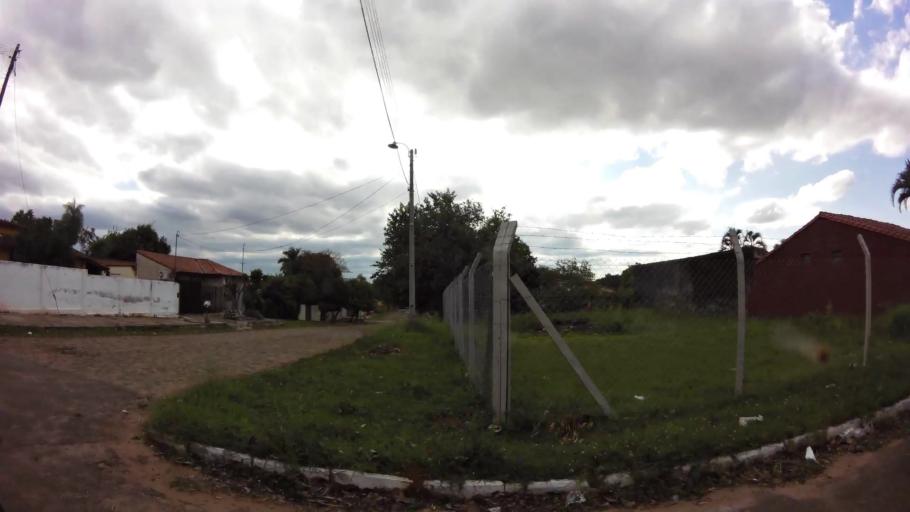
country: PY
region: Central
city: San Lorenzo
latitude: -25.2685
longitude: -57.5047
